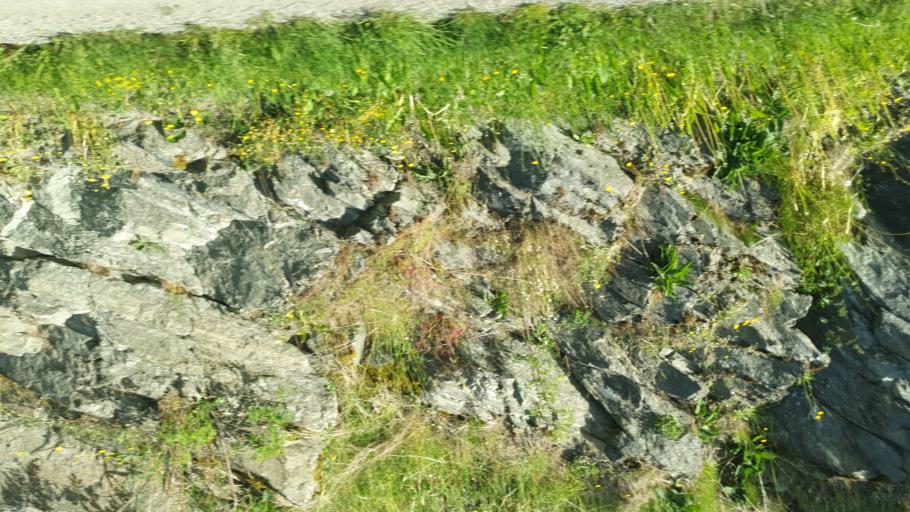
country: NO
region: Sor-Trondelag
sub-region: Rissa
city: Rissa
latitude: 63.4968
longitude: 10.0987
